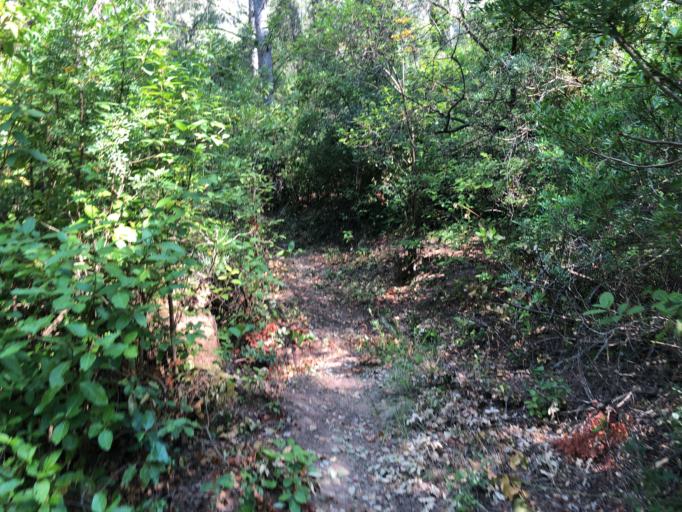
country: ES
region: Catalonia
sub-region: Provincia de Barcelona
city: Corbera de Llobregat
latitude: 41.4216
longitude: 1.9100
